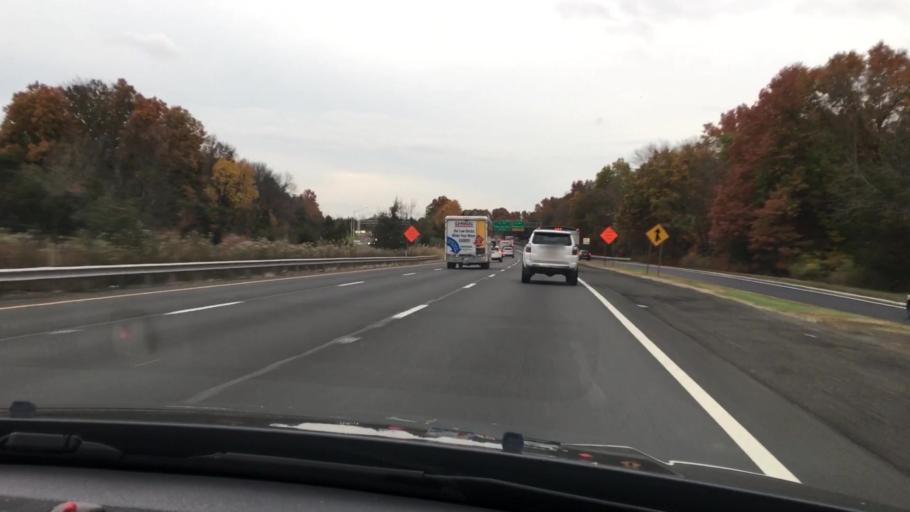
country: US
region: New Jersey
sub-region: Somerset County
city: Bedminster
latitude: 40.6573
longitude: -74.6450
